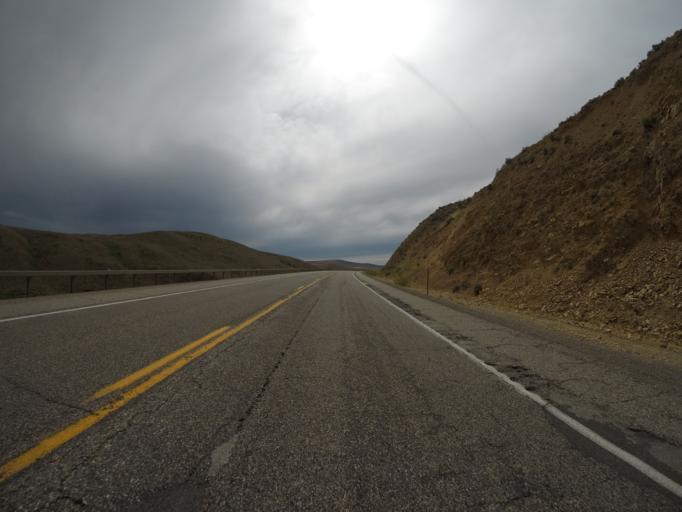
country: US
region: Wyoming
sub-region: Lincoln County
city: Kemmerer
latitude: 41.8238
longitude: -110.8564
